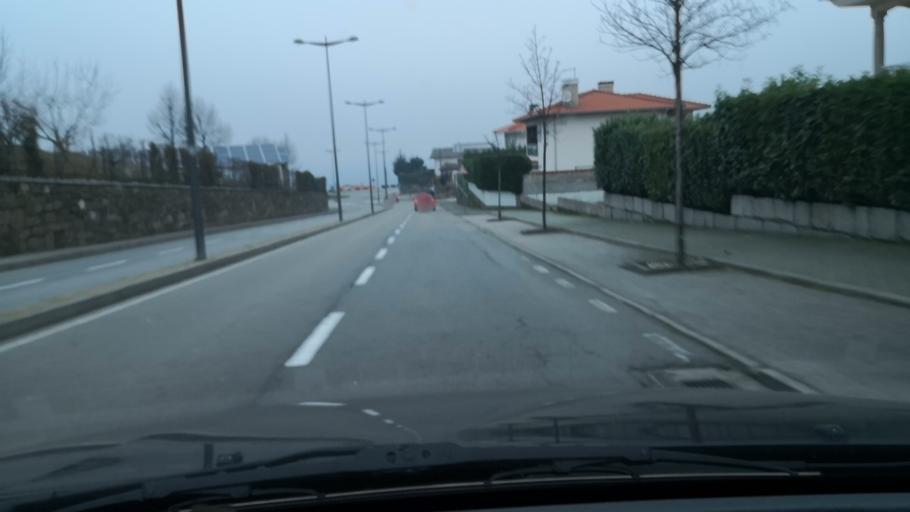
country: PT
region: Viseu
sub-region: Lamego
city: Lamego
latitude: 41.1103
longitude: -7.8051
